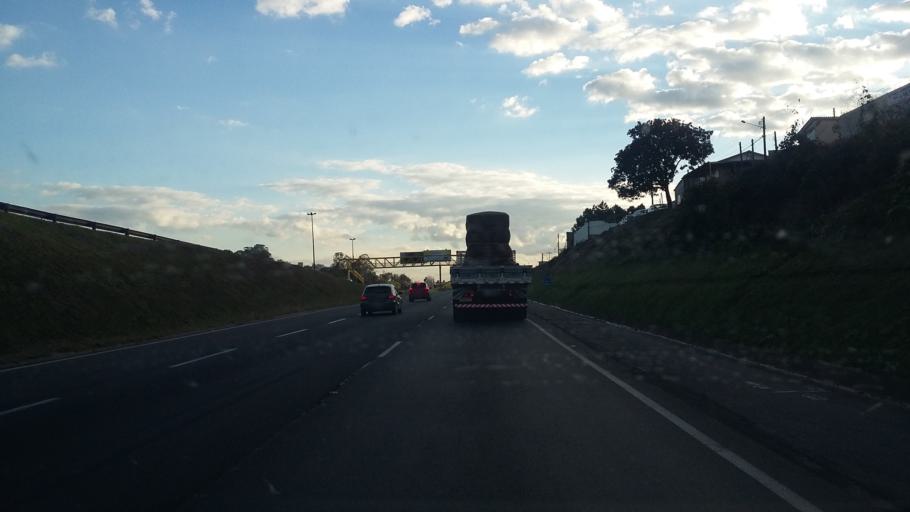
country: BR
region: Parana
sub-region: Curitiba
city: Curitiba
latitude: -25.4326
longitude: -49.4029
